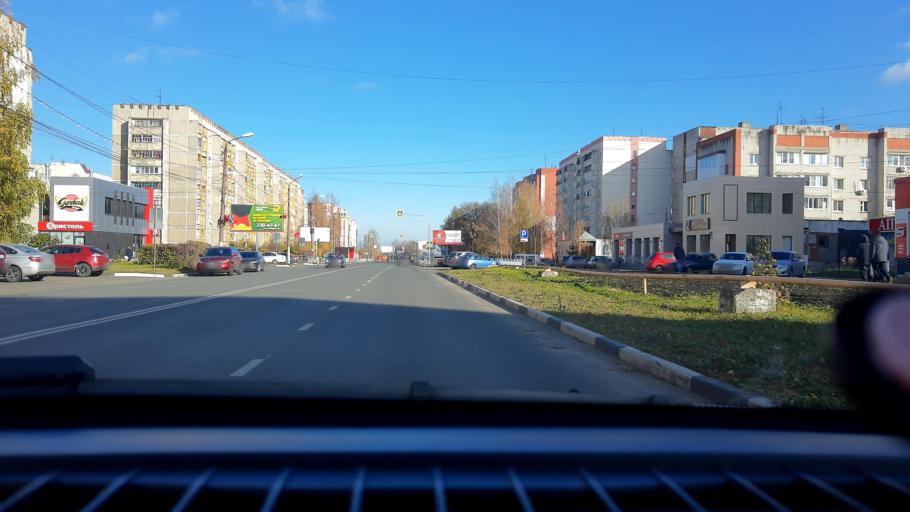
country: RU
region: Nizjnij Novgorod
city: Kstovo
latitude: 56.1533
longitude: 44.2098
